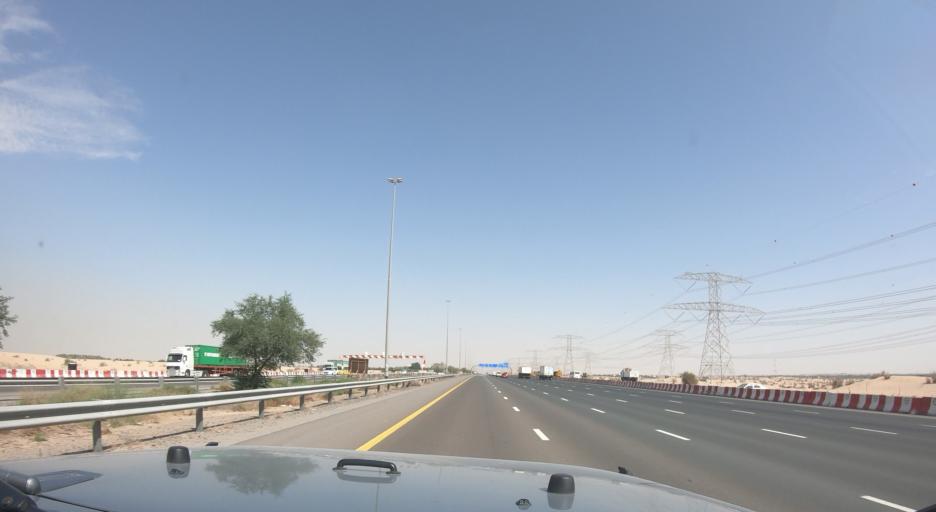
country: AE
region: Ash Shariqah
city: Sharjah
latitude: 25.1808
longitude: 55.5192
